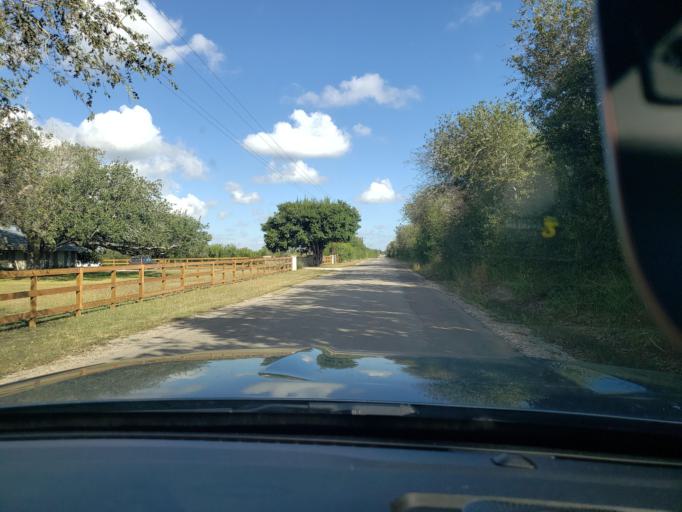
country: US
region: Texas
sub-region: Bee County
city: Beeville
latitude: 28.4514
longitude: -97.7174
